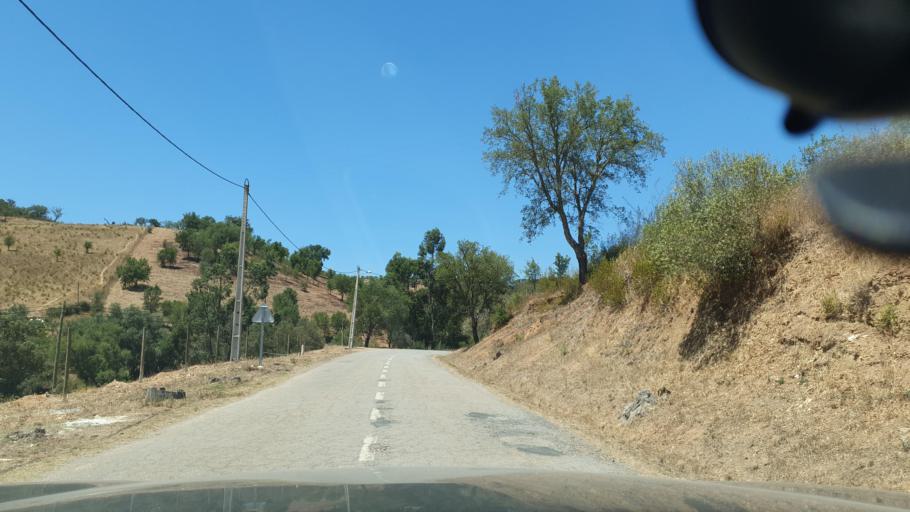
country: PT
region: Beja
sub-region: Odemira
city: Odemira
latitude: 37.5893
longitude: -8.4916
